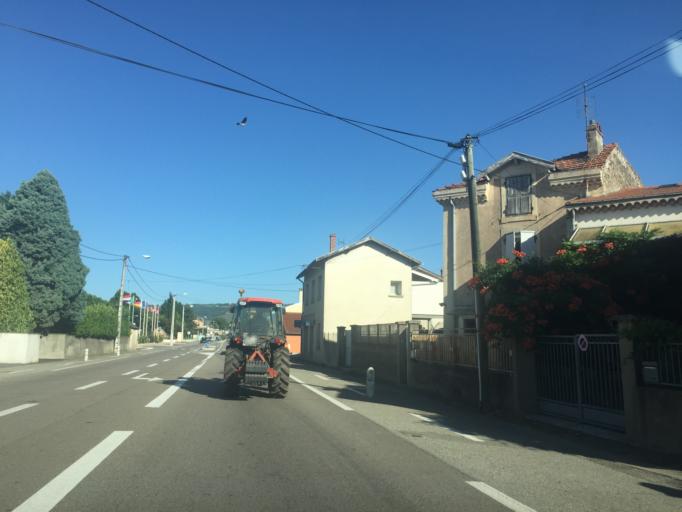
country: FR
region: Rhone-Alpes
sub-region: Departement de l'Ardeche
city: Tournon-sur-Rhone
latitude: 45.0664
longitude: 4.8524
